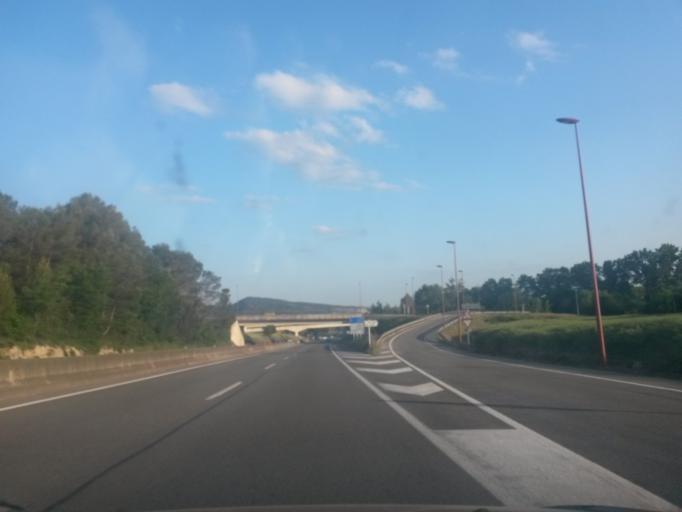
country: ES
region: Catalonia
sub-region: Provincia de Girona
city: Sarria de Ter
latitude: 42.0434
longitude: 2.8209
